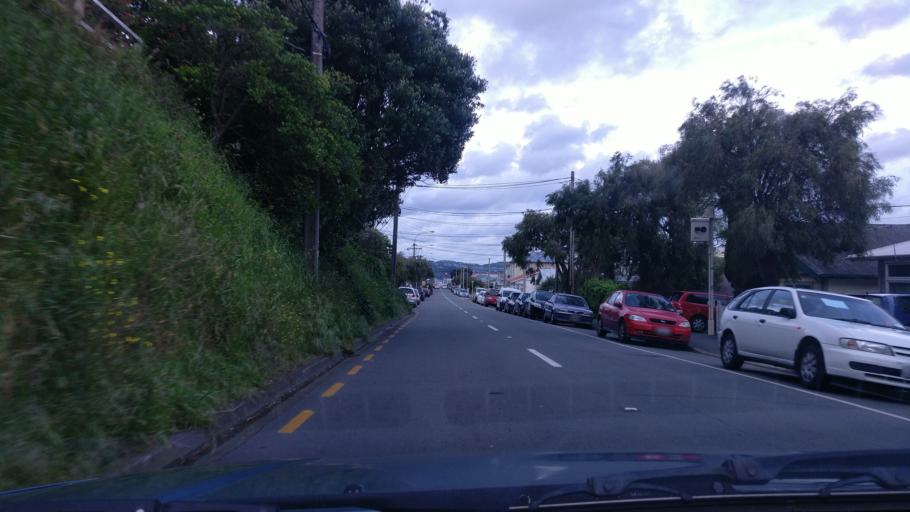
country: NZ
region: Wellington
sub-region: Wellington City
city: Brooklyn
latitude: -41.3131
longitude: 174.7760
